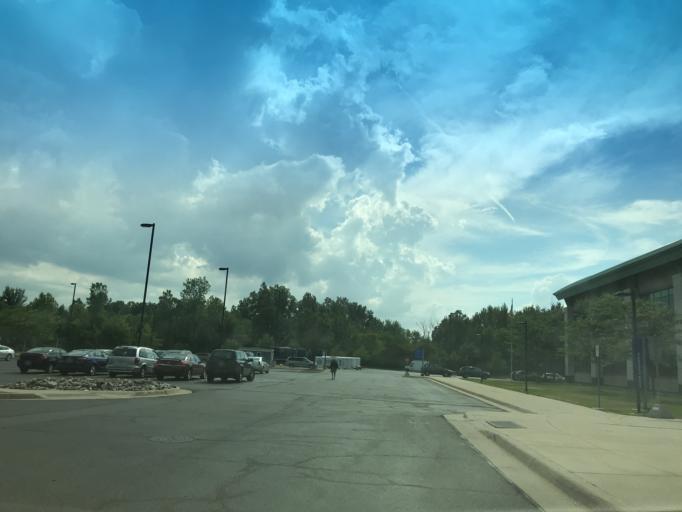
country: US
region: Michigan
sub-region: Eaton County
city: Waverly
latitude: 42.7176
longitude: -84.6306
